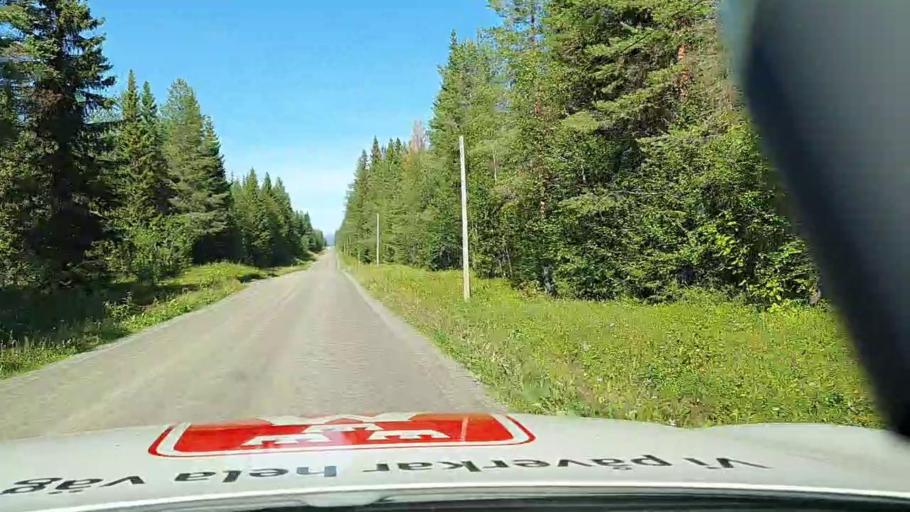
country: SE
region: Jaemtland
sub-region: Krokoms Kommun
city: Krokom
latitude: 63.6894
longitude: 14.6058
